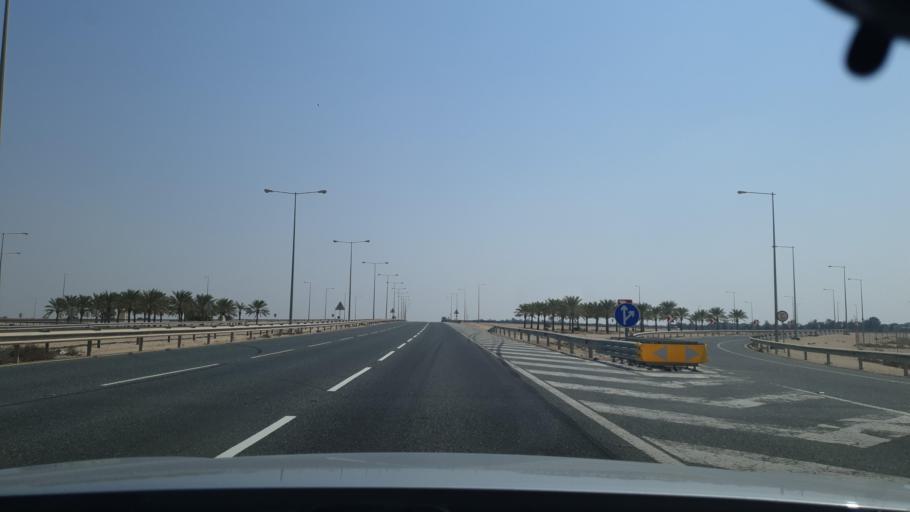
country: QA
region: Al Khawr
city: Al Khawr
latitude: 25.7886
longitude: 51.3935
